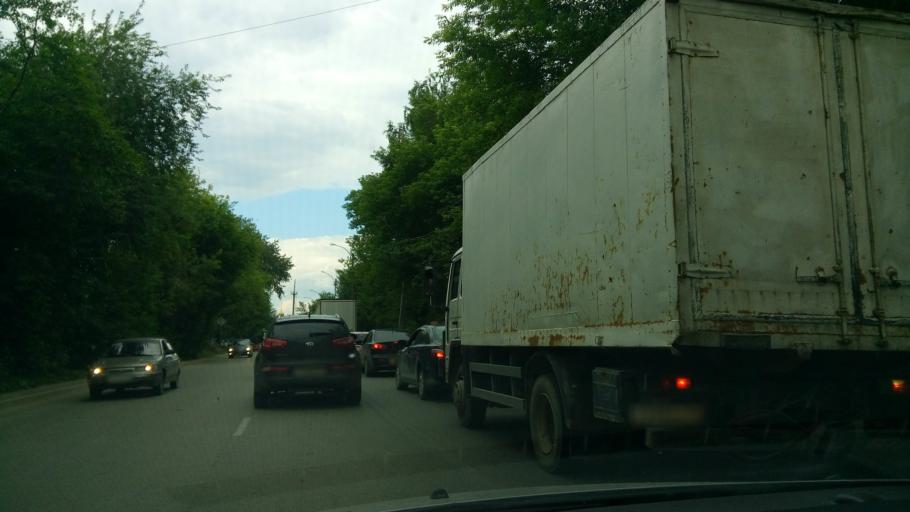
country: RU
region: Sverdlovsk
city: Yekaterinburg
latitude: 56.8737
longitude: 60.6881
